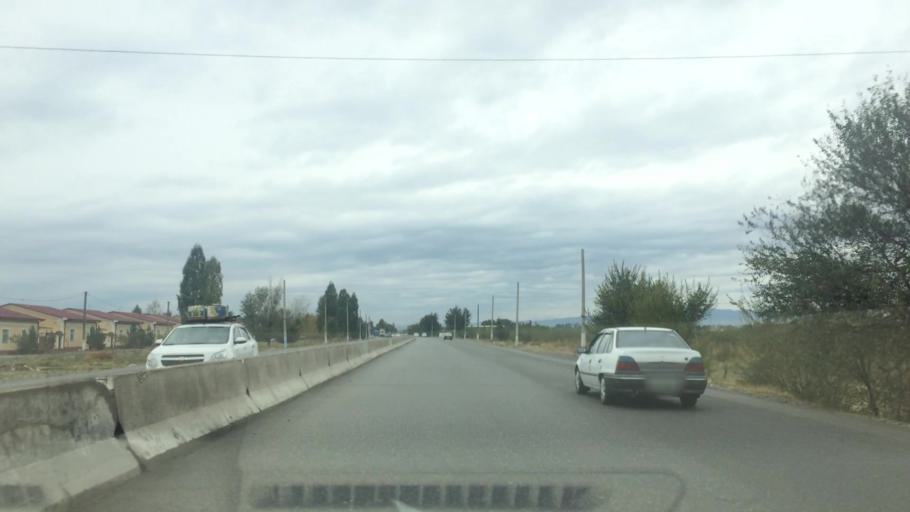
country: UZ
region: Jizzax
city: Jizzax
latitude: 40.0185
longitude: 67.6100
